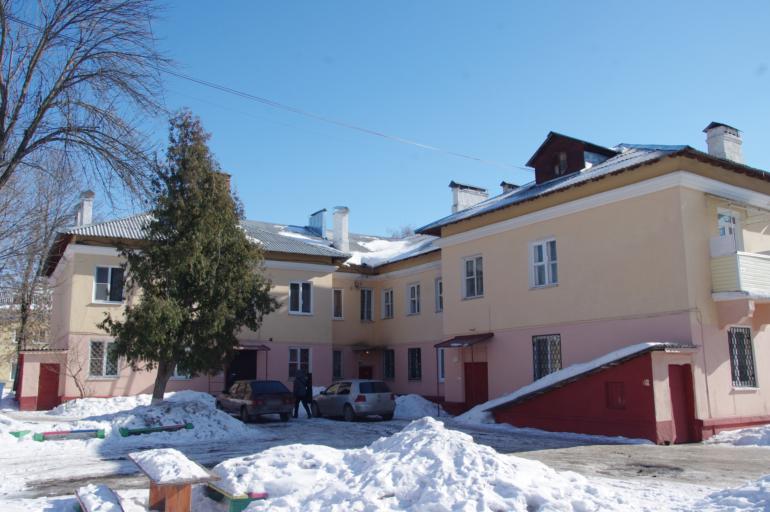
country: RU
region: Moskovskaya
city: Kolomna
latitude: 55.0753
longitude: 38.8076
